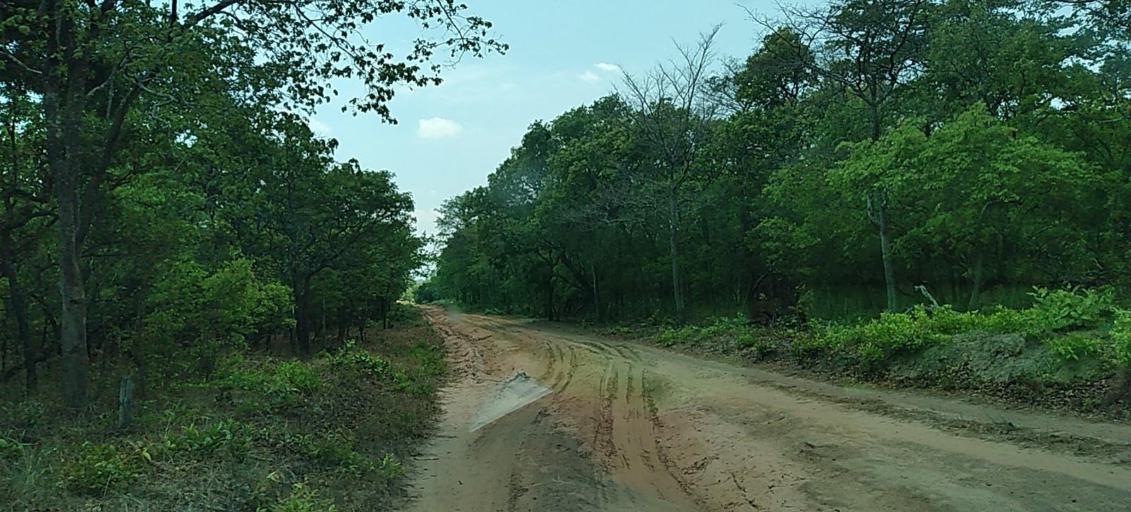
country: CD
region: Katanga
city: Kolwezi
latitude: -11.3498
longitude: 25.2141
